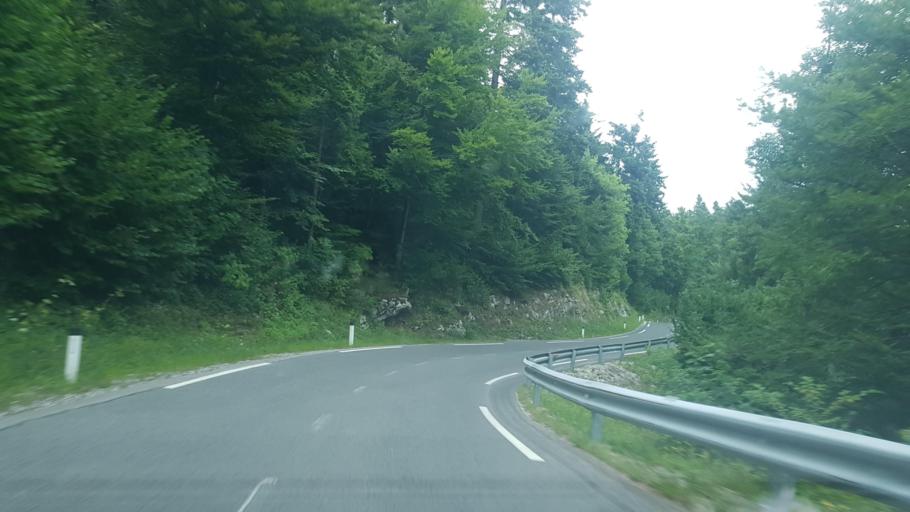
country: SI
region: Logatec
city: Logatec
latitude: 45.8678
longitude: 14.1241
